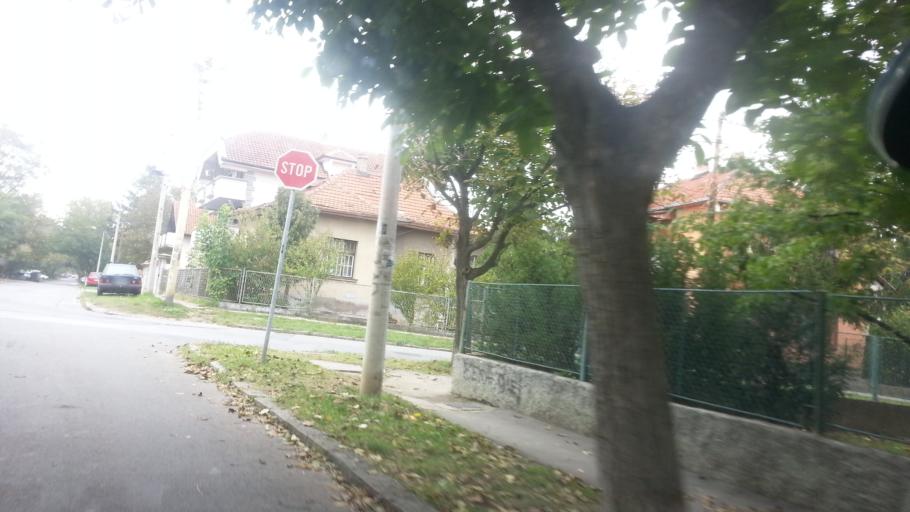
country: RS
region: Central Serbia
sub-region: Belgrade
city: Zemun
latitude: 44.8354
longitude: 20.3956
